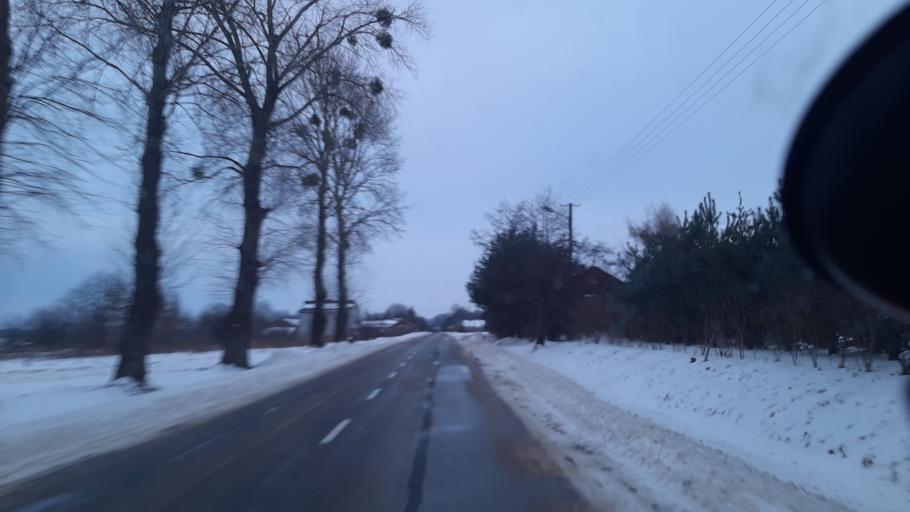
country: PL
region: Lublin Voivodeship
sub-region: Powiat lubelski
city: Jastkow
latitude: 51.3441
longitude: 22.4003
